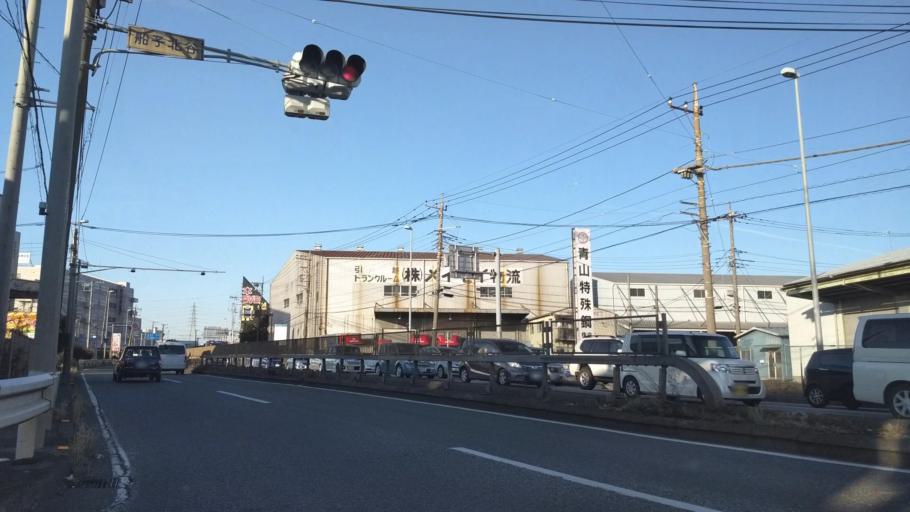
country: JP
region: Kanagawa
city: Atsugi
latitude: 35.4277
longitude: 139.3571
